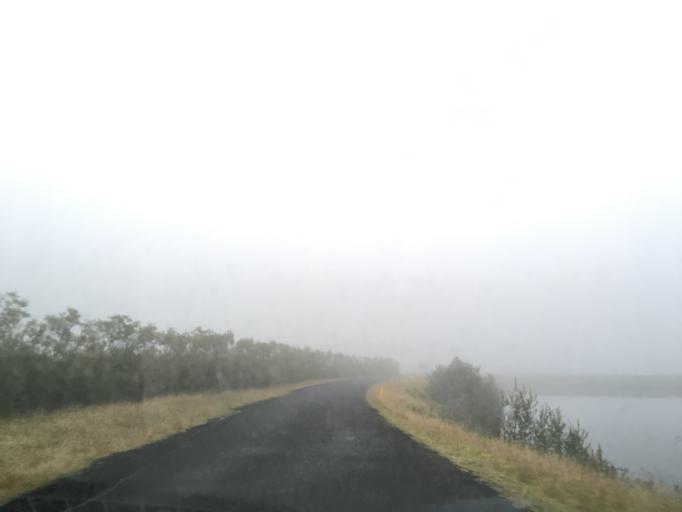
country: IS
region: South
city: Vestmannaeyjar
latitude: 63.4255
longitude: -18.9064
